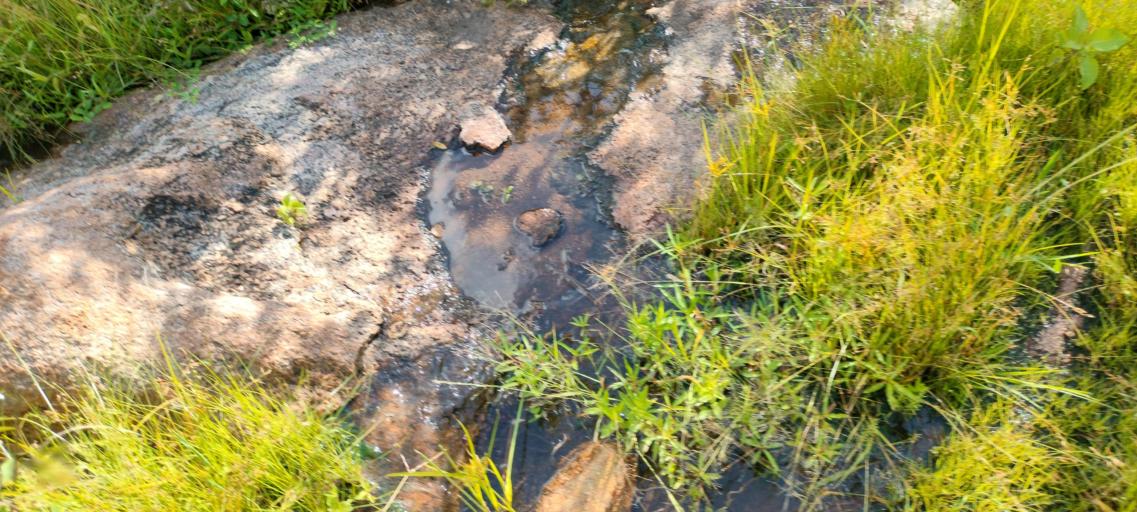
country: IN
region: Telangana
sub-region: Mahbubnagar
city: Farrukhnagar
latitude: 16.8942
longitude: 78.4919
